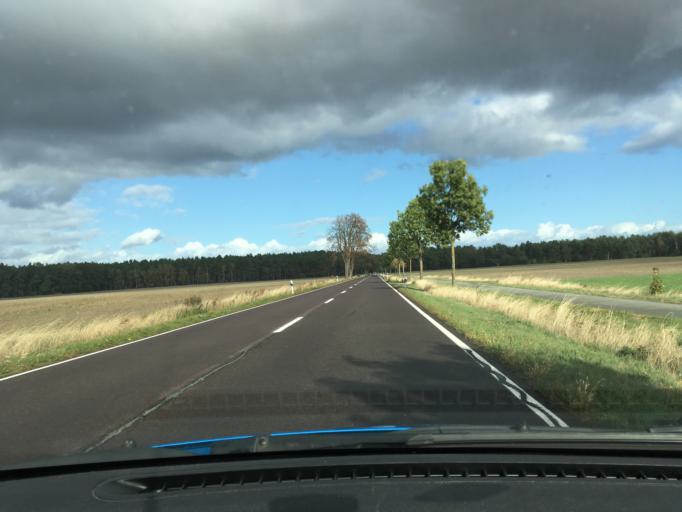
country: DE
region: Saxony-Anhalt
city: Pretzier
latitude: 52.8482
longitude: 11.3492
